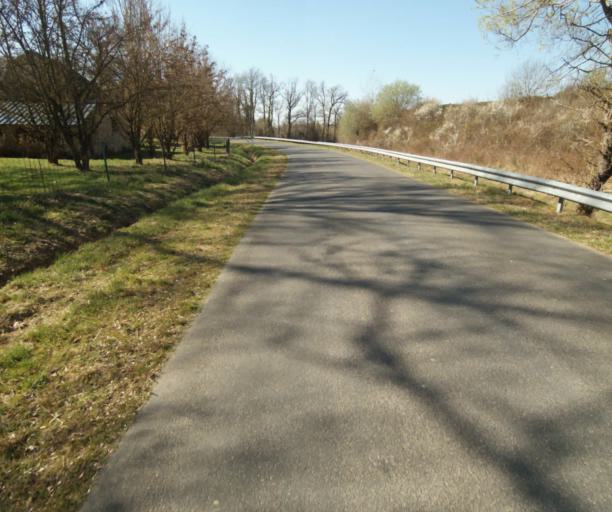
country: FR
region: Limousin
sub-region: Departement de la Correze
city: Saint-Mexant
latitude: 45.2845
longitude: 1.6201
